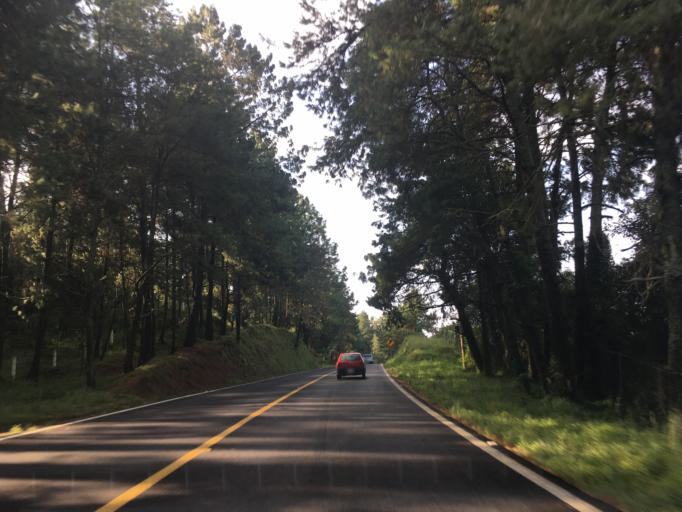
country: MX
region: Michoacan
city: Tingambato
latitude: 19.5035
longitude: -101.8350
